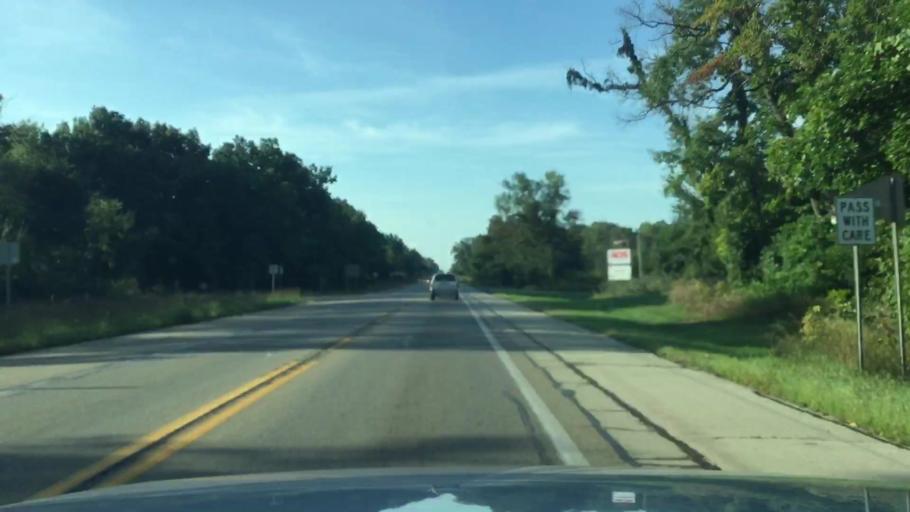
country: US
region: Michigan
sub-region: Jackson County
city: Vandercook Lake
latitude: 42.1146
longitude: -84.3641
